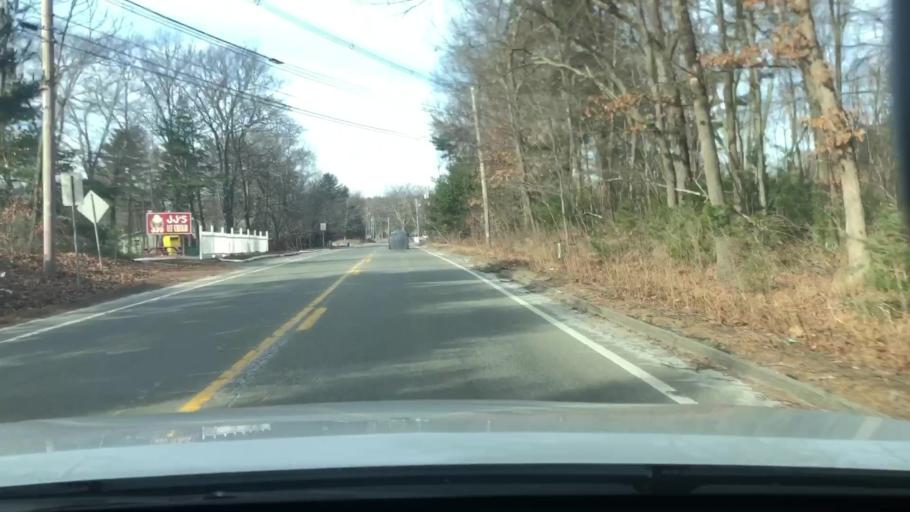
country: US
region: Massachusetts
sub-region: Worcester County
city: Upton
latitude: 42.1591
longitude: -71.5823
